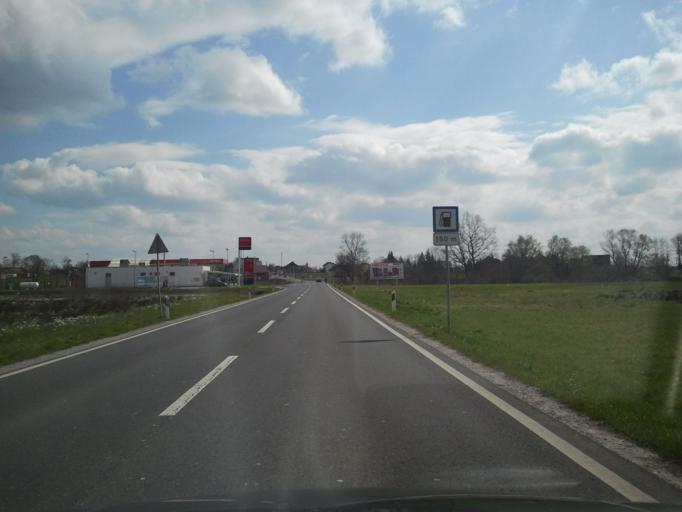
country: HR
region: Zagrebacka
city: Jastrebarsko
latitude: 45.6899
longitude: 15.7244
